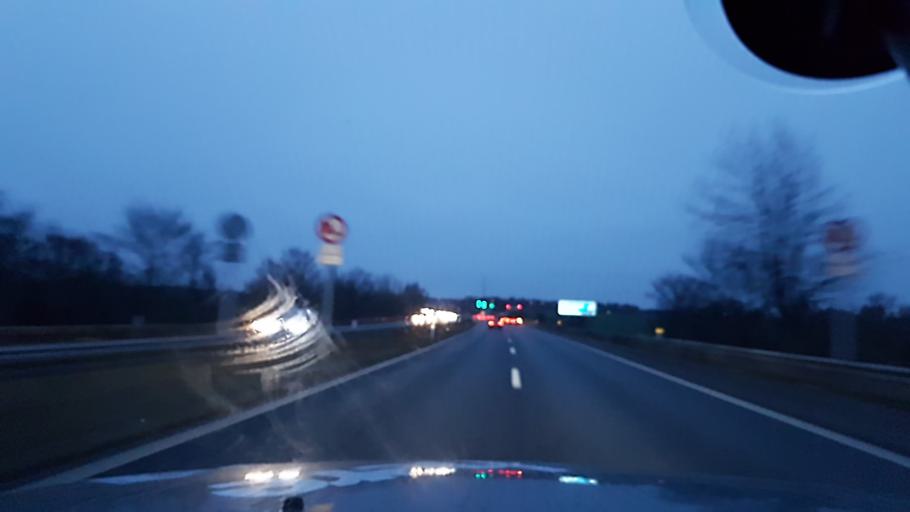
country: DK
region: Zealand
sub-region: Koge Kommune
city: Ejby
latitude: 55.4697
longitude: 12.1245
